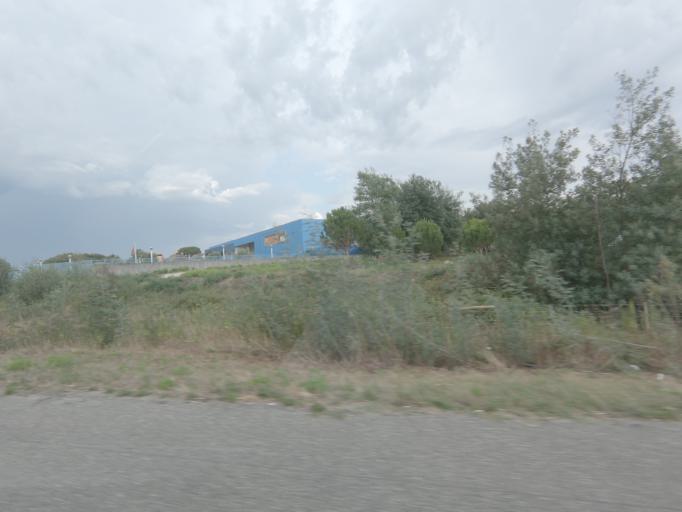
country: PT
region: Viseu
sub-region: Concelho de Tondela
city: Tondela
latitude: 40.5230
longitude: -8.0912
